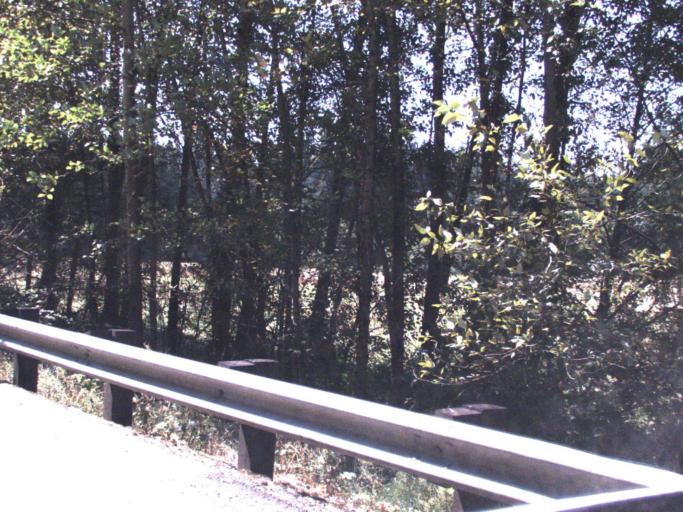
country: US
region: Washington
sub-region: King County
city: Ames Lake
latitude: 47.5977
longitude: -121.9616
